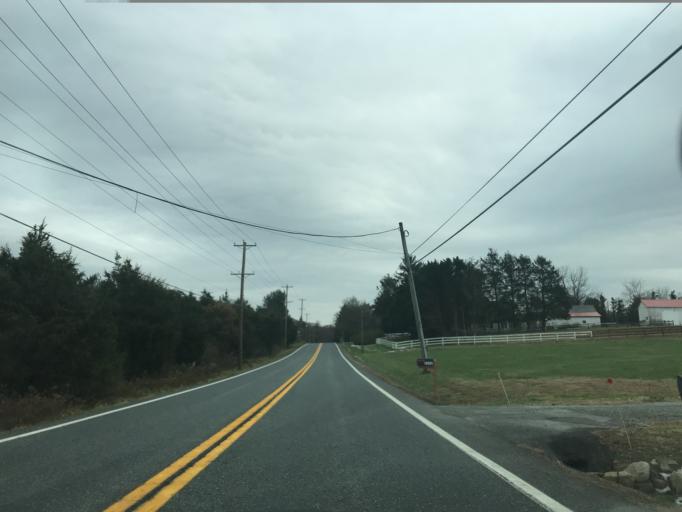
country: US
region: Pennsylvania
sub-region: York County
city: Susquehanna Trails
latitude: 39.6660
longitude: -76.3497
